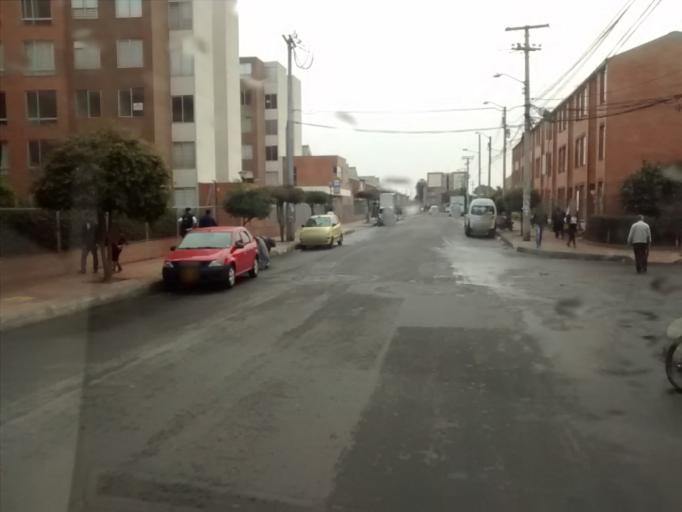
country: CO
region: Cundinamarca
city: Cota
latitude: 4.7573
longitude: -74.1063
